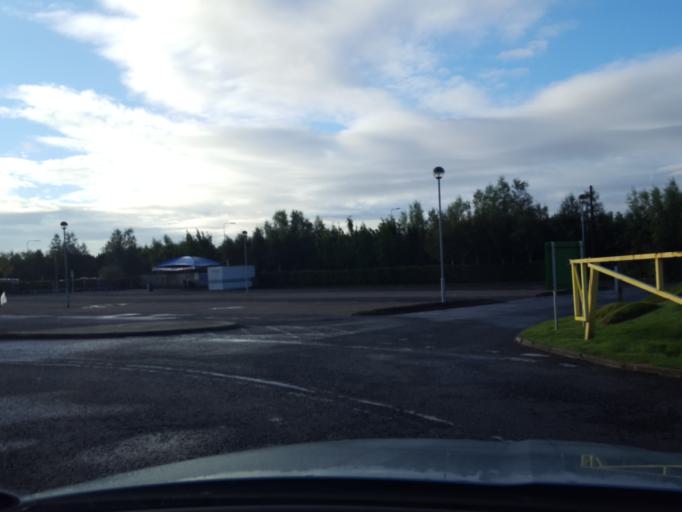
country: GB
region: Scotland
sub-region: Fife
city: Crossgates
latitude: 56.0762
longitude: -3.3970
